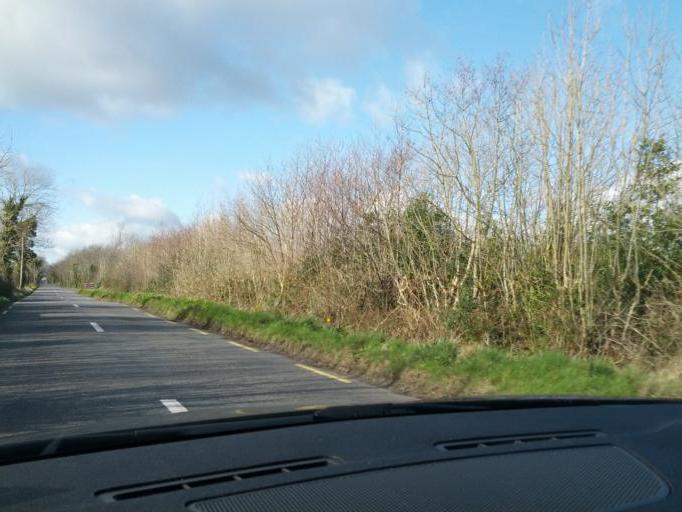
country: IE
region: Connaught
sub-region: County Galway
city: Athenry
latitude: 53.4955
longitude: -8.5679
